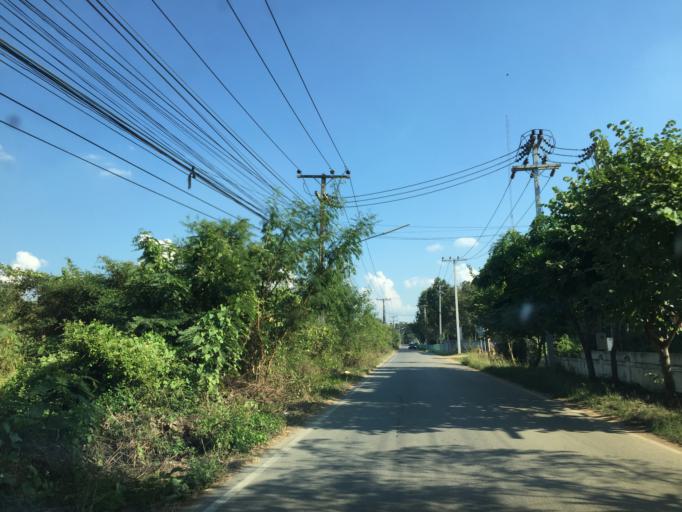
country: TH
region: Lamphun
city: Lamphun
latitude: 18.5711
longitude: 99.0396
